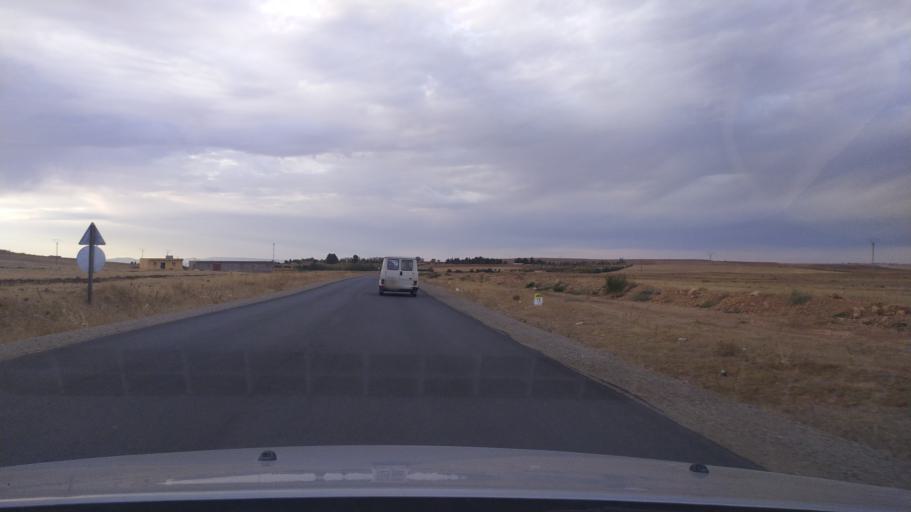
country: DZ
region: Tiaret
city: Frenda
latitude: 35.0154
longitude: 1.1115
